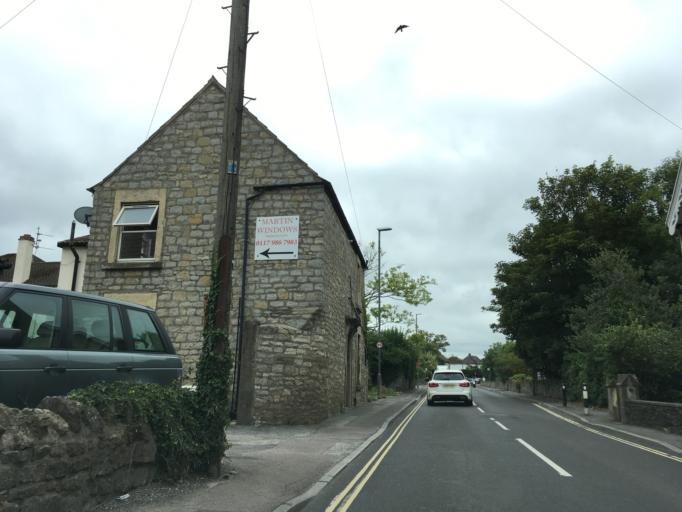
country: GB
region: England
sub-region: Bath and North East Somerset
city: Keynsham
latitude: 51.4115
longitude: -2.4935
